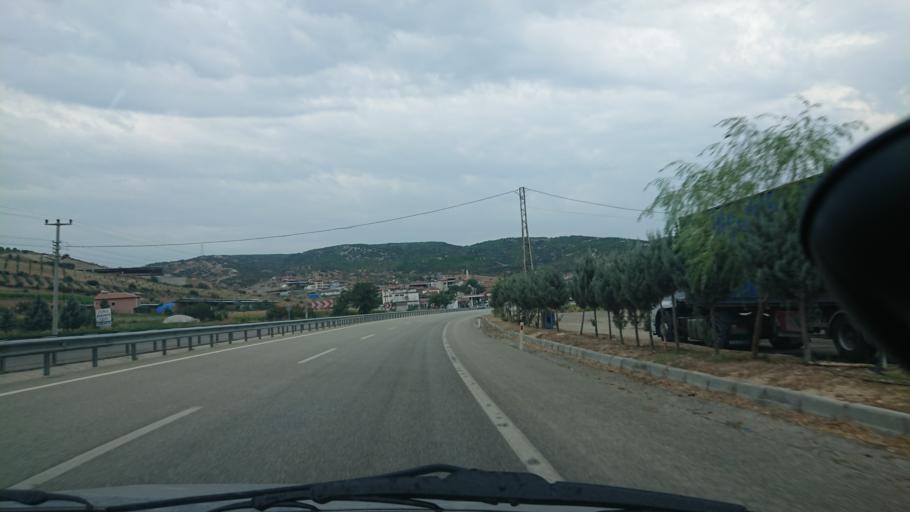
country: TR
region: Manisa
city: Selendi
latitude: 38.5950
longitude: 28.8127
